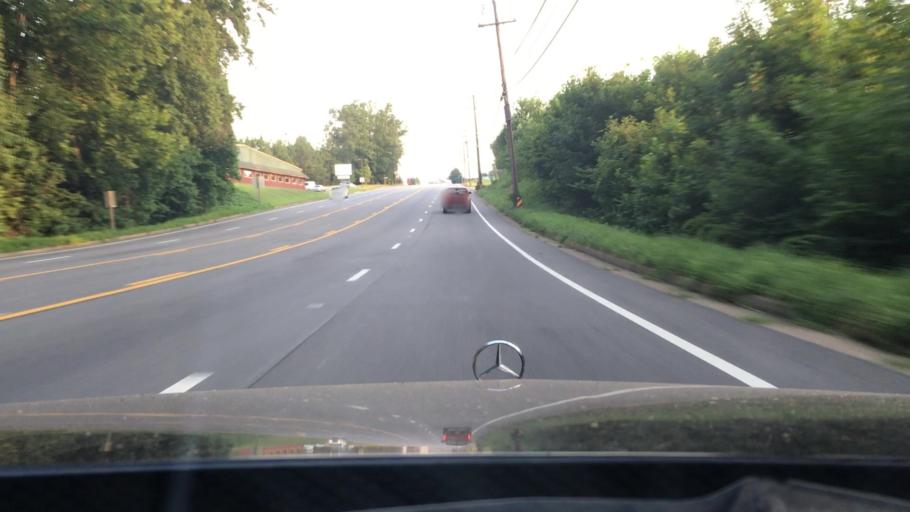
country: US
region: Virginia
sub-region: Pittsylvania County
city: Mount Hermon
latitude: 36.6462
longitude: -79.3814
